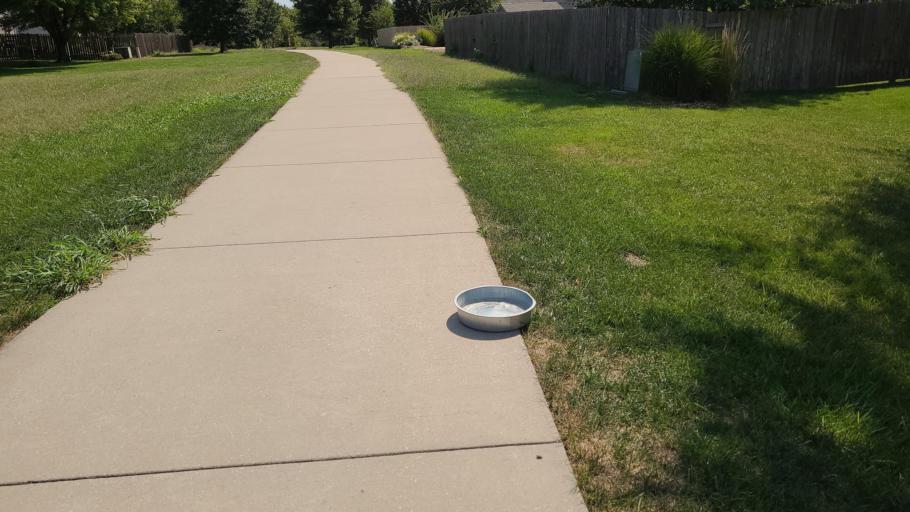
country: US
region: Kansas
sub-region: Douglas County
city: Lawrence
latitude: 38.9654
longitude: -95.3185
